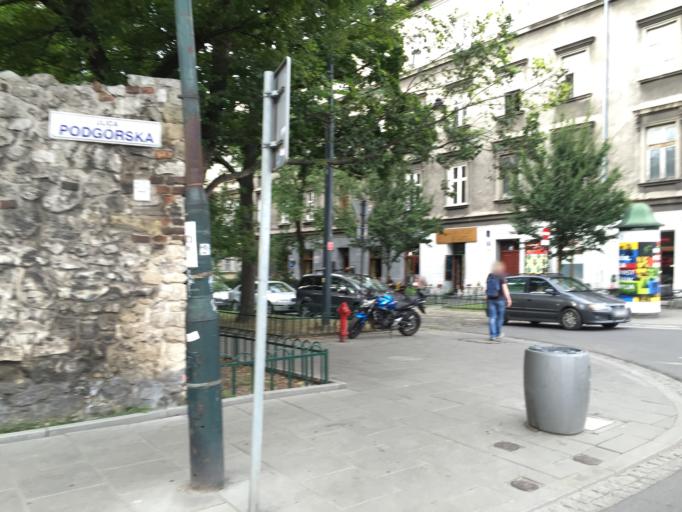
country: PL
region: Lesser Poland Voivodeship
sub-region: Krakow
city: Krakow
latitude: 50.0471
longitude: 19.9467
